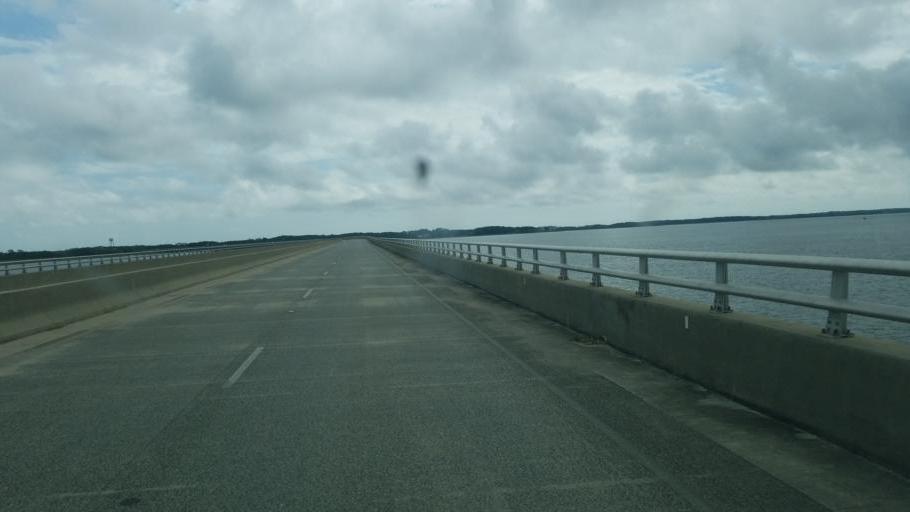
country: US
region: North Carolina
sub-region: Dare County
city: Manteo
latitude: 35.8823
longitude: -75.6880
